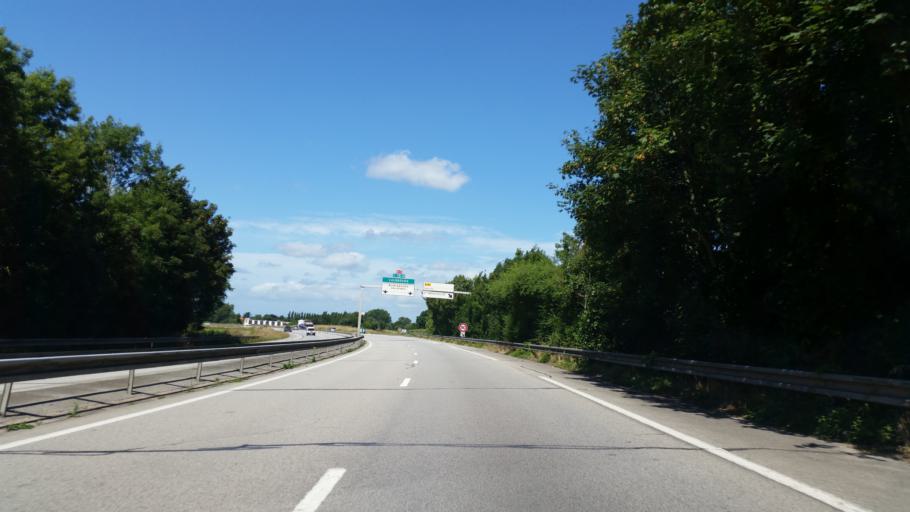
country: FR
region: Lower Normandy
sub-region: Departement de la Manche
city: Sainte-Mere-Eglise
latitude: 49.3996
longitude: -1.3077
